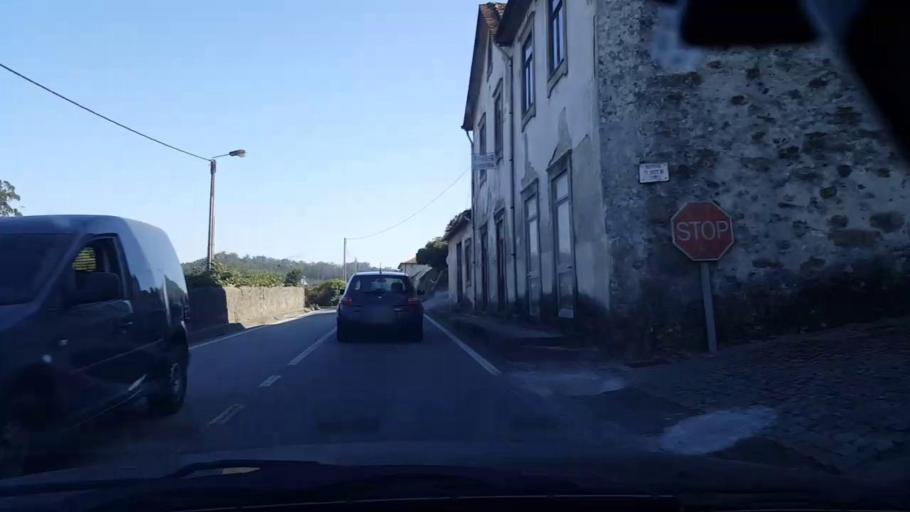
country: PT
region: Porto
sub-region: Vila do Conde
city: Arvore
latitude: 41.3313
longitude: -8.6627
